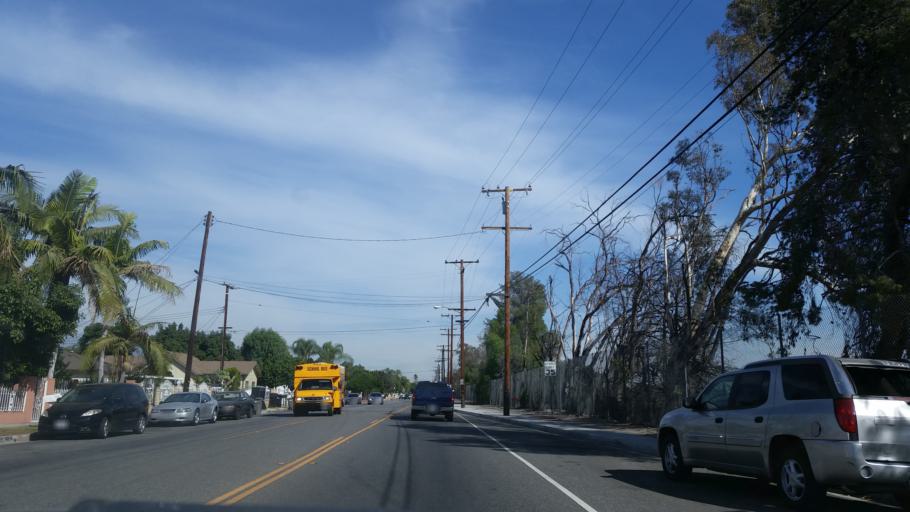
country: US
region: California
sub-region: Los Angeles County
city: Baldwin Park
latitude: 34.0996
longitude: -117.9547
